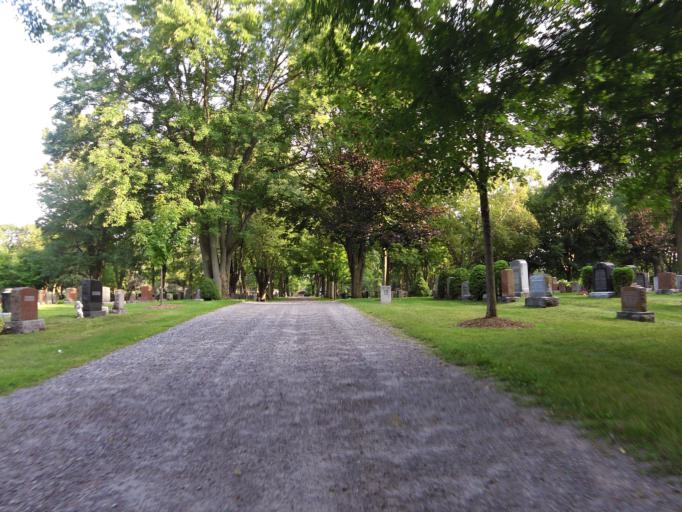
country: CA
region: Ontario
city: Bells Corners
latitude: 45.3423
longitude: -75.7814
